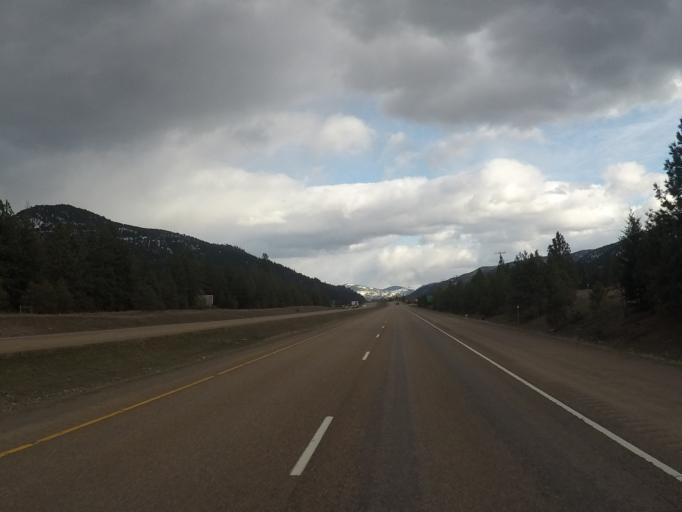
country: US
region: Montana
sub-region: Missoula County
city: Bonner-West Riverside
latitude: 46.8405
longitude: -113.8375
